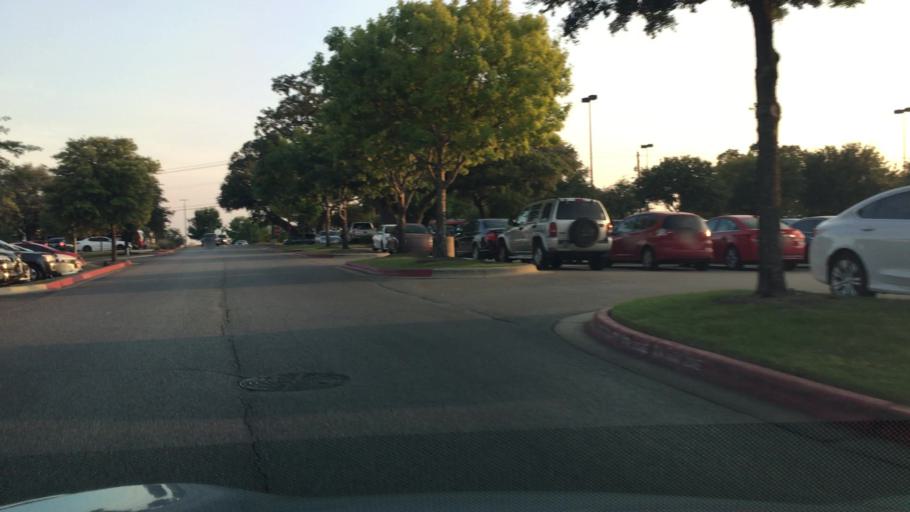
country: US
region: Texas
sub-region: Travis County
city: Onion Creek
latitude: 30.1637
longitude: -97.7895
